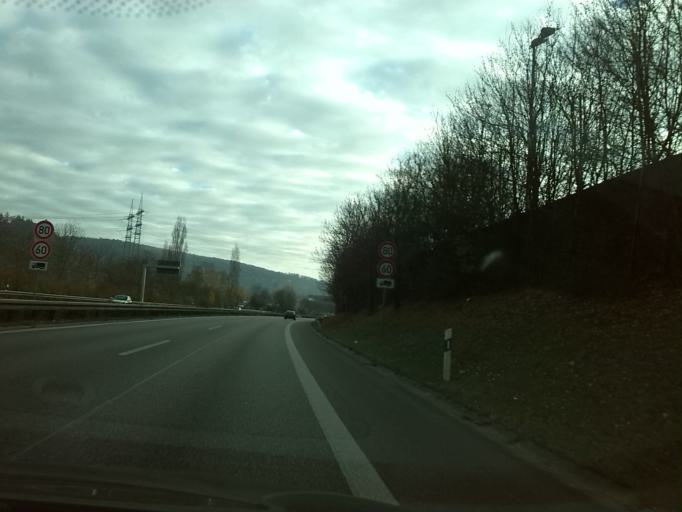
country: DE
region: Baden-Wuerttemberg
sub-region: Regierungsbezirk Stuttgart
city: Deizisau
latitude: 48.7165
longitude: 9.3866
